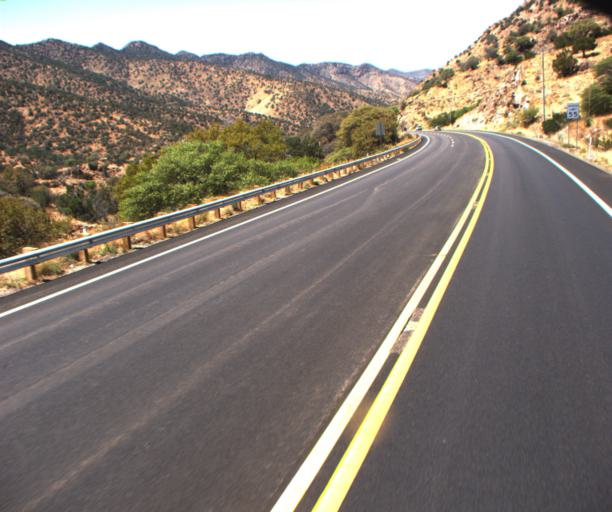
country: US
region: Arizona
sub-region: Cochise County
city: Bisbee
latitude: 31.4649
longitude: -109.9512
